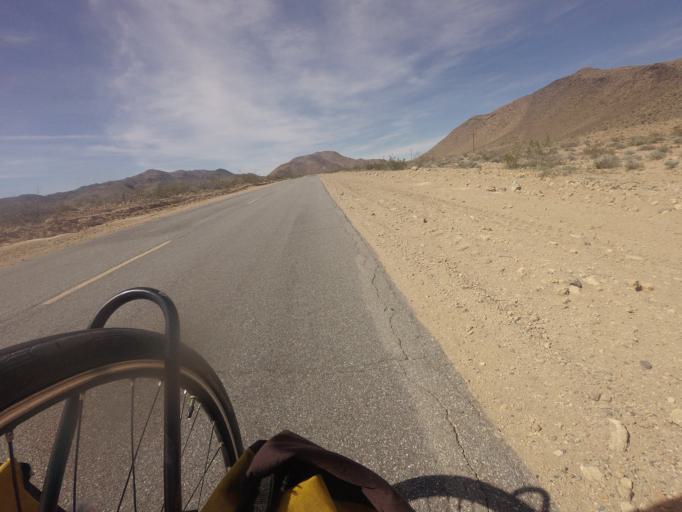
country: US
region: California
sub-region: San Bernardino County
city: Searles Valley
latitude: 35.5757
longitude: -117.4523
